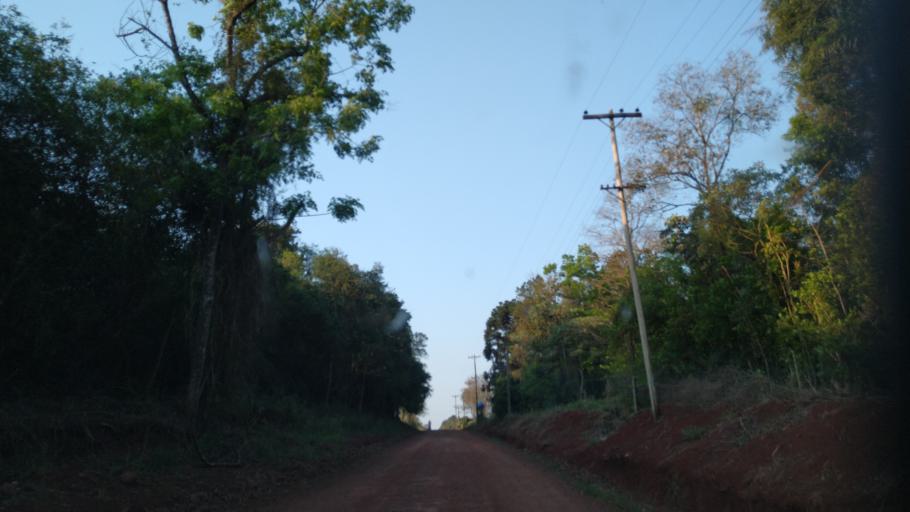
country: AR
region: Misiones
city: Jardin America
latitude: -27.0884
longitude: -55.2778
